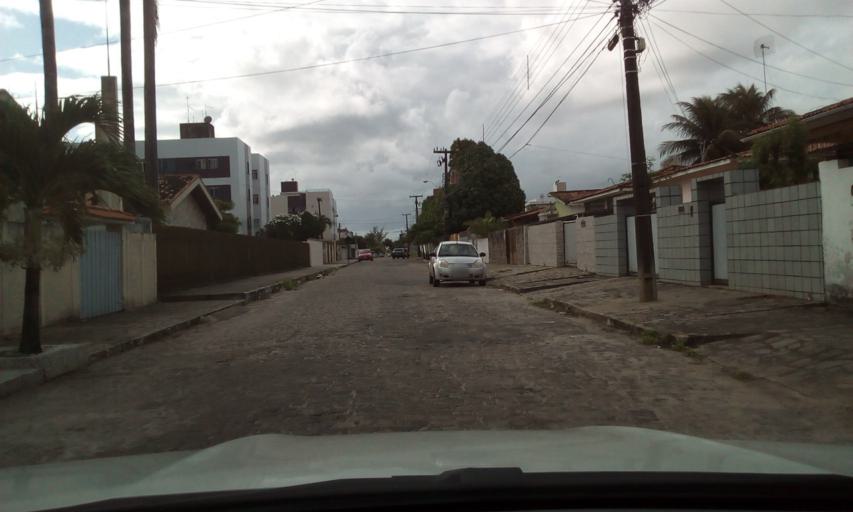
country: BR
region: Paraiba
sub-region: Joao Pessoa
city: Joao Pessoa
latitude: -7.1621
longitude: -34.8724
